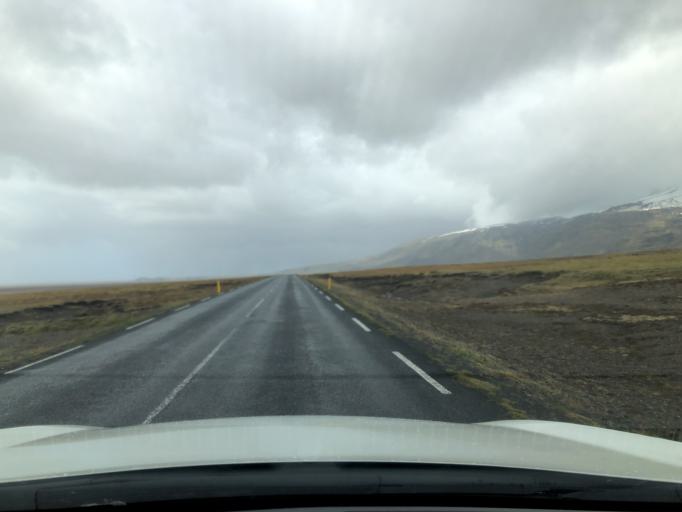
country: IS
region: East
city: Hoefn
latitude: 63.9282
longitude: -16.4744
